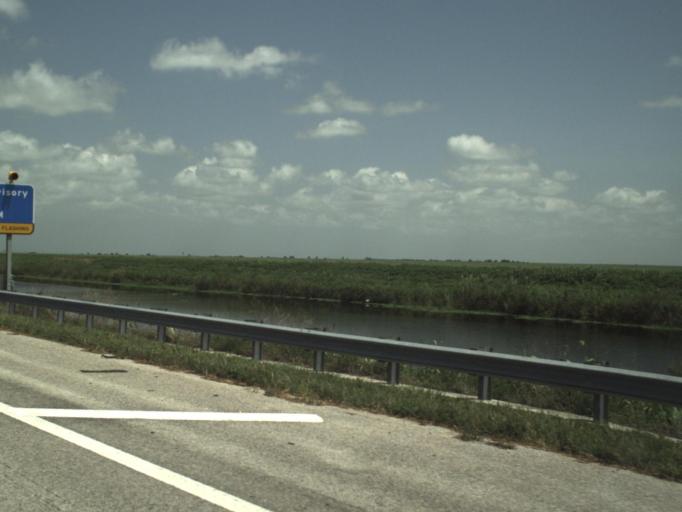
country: US
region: Florida
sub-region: Palm Beach County
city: Belle Glade Camp
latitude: 26.5406
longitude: -80.6971
